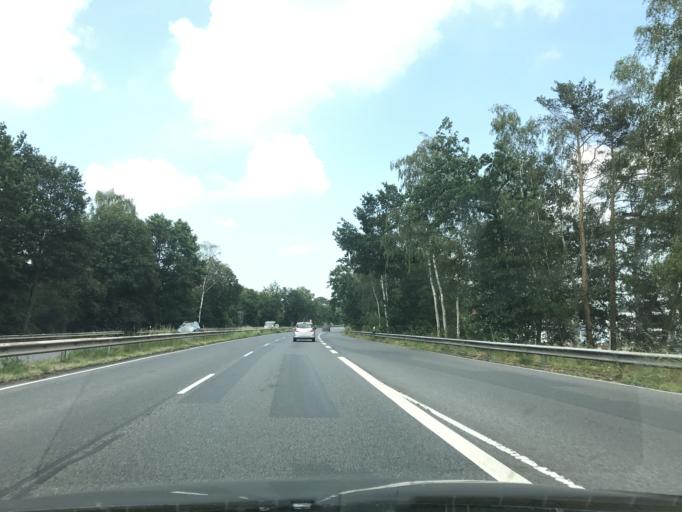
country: DE
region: Lower Saxony
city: Varel
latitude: 53.3987
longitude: 8.1164
